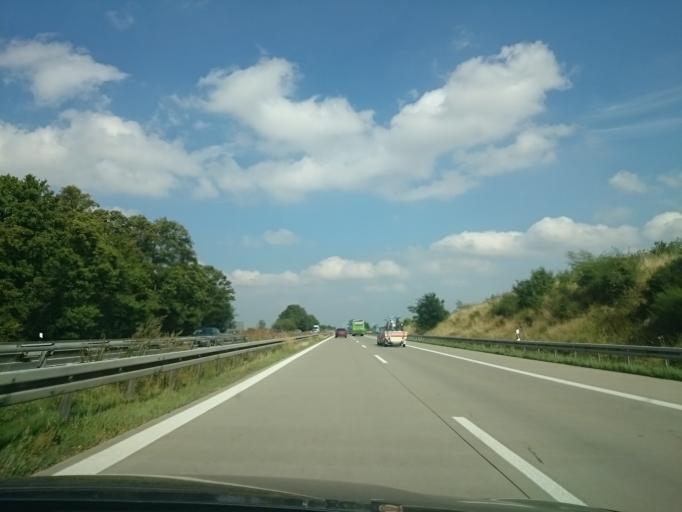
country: DE
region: Brandenburg
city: Gramzow
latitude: 53.2245
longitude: 13.9794
